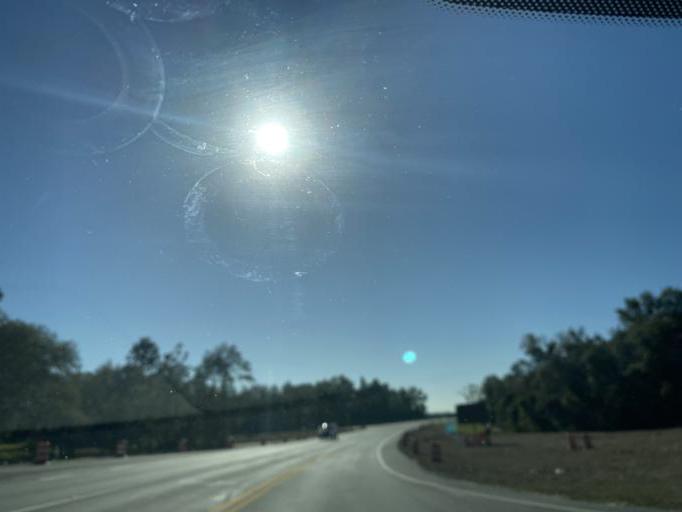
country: US
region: Florida
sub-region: Lake County
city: Mount Plymouth
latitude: 28.8312
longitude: -81.5220
